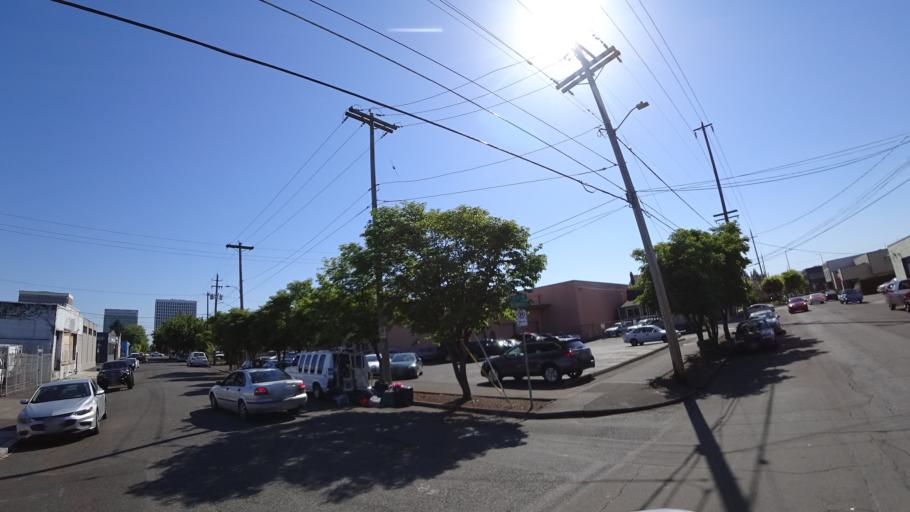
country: US
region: Oregon
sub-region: Multnomah County
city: Portland
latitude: 45.5365
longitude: -122.6596
